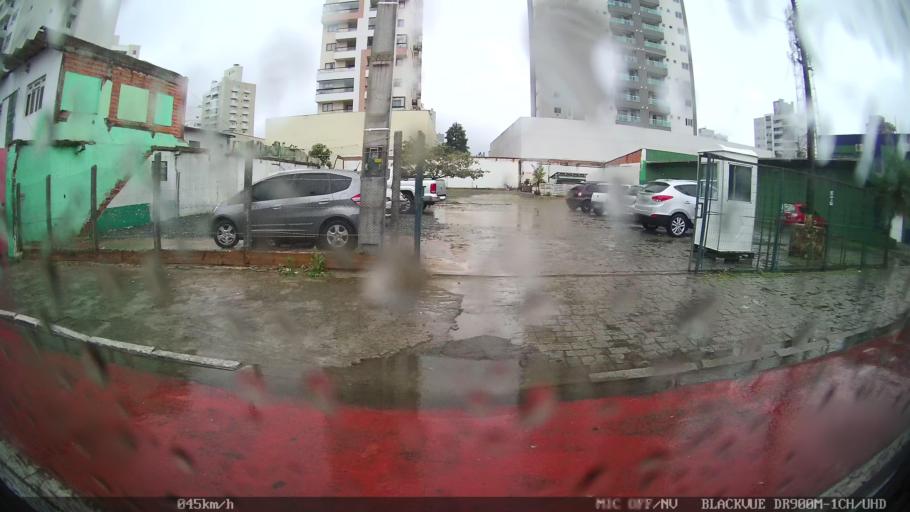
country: BR
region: Santa Catarina
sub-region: Itajai
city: Itajai
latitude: -26.9075
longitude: -48.6749
